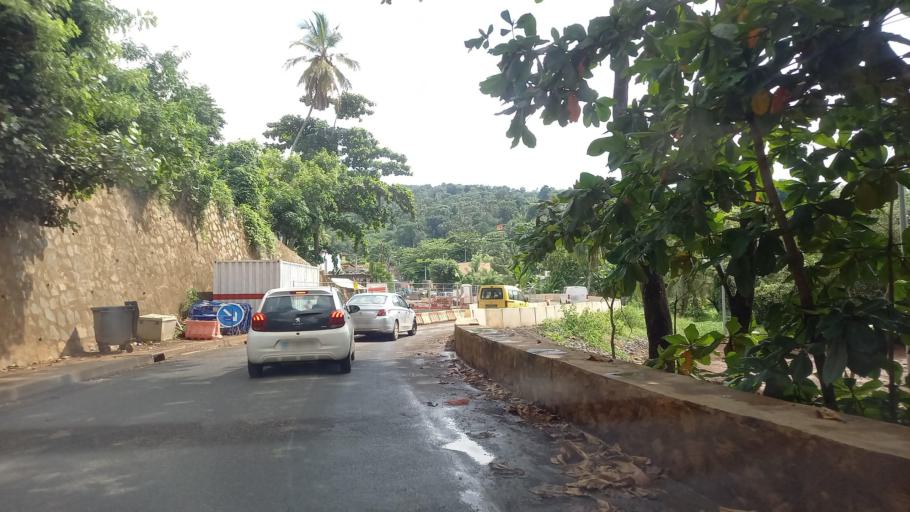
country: YT
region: Chiconi
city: Chiconi
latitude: -12.8431
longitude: 45.1167
